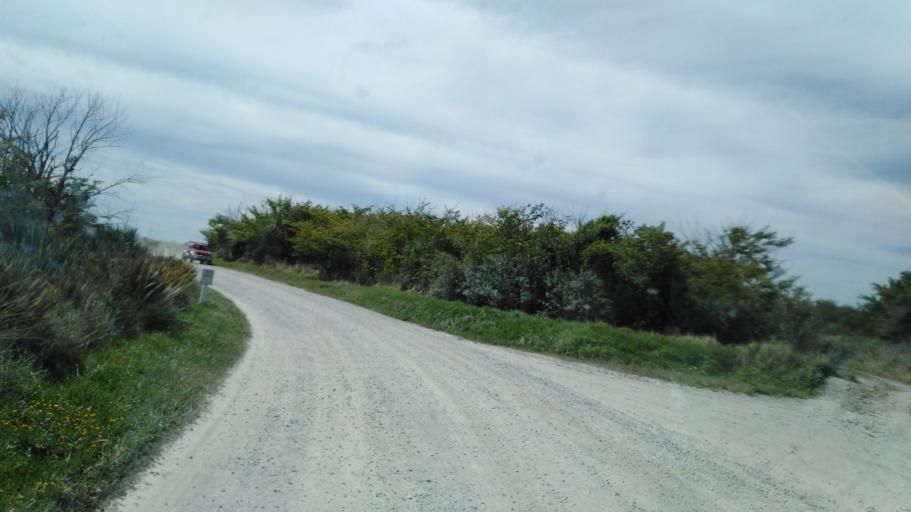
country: NZ
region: West Coast
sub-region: Buller District
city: Westport
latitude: -41.7359
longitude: 171.6053
